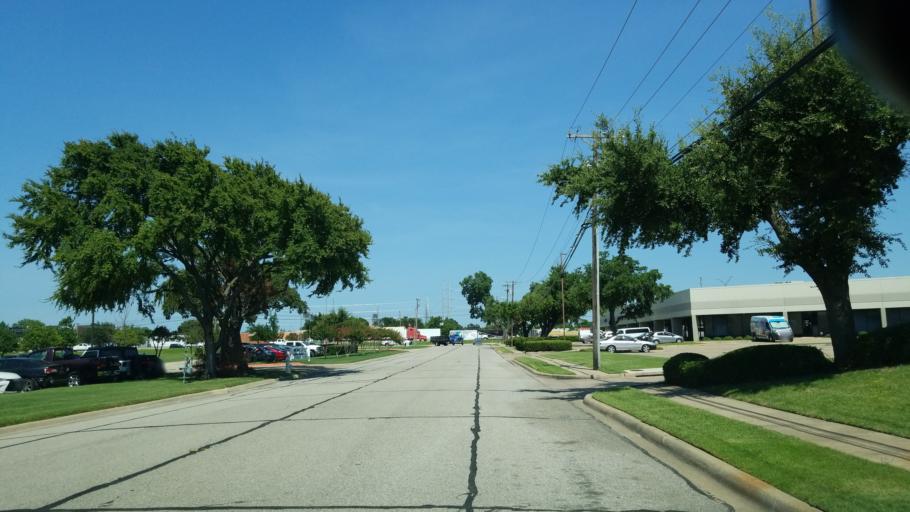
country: US
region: Texas
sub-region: Dallas County
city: Farmers Branch
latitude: 32.9262
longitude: -96.9030
